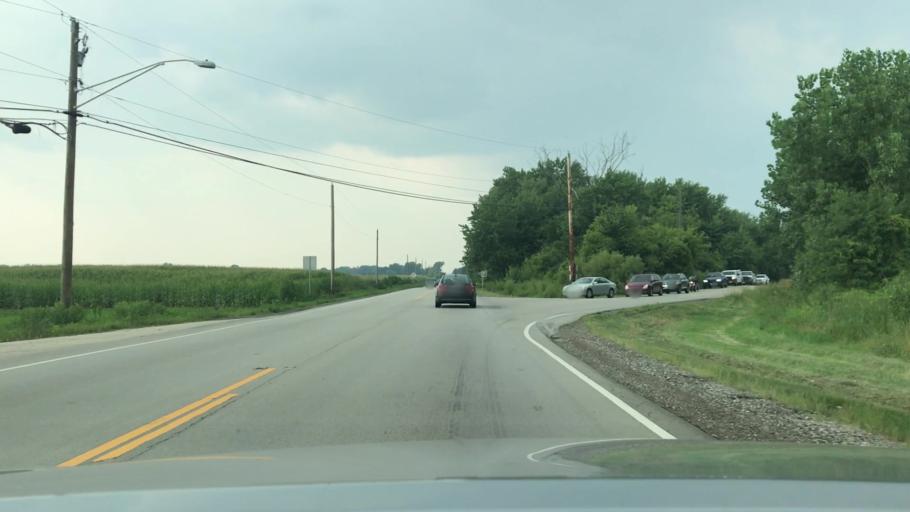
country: US
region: Illinois
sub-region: Will County
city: Plainfield
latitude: 41.6845
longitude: -88.2534
